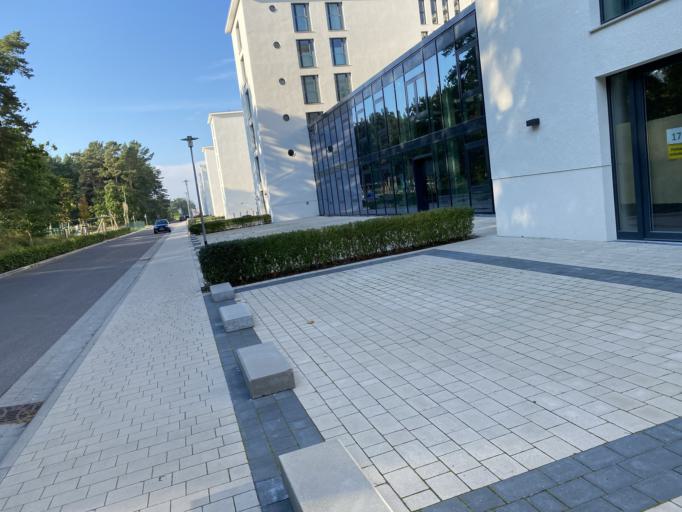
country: DE
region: Mecklenburg-Vorpommern
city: Ostseebad Binz
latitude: 54.4273
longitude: 13.5830
